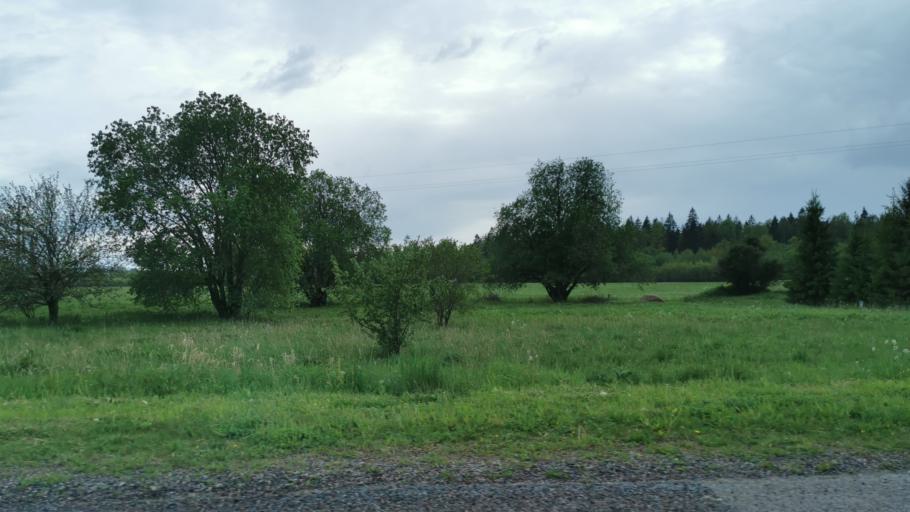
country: EE
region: Laeaene-Virumaa
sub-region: Rakvere linn
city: Rakvere
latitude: 59.2741
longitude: 26.3510
